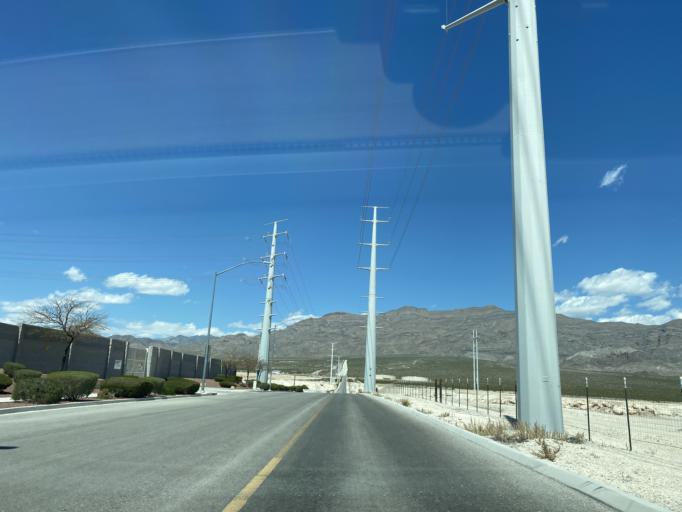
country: US
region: Nevada
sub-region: Clark County
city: North Las Vegas
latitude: 36.3230
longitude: -115.2071
